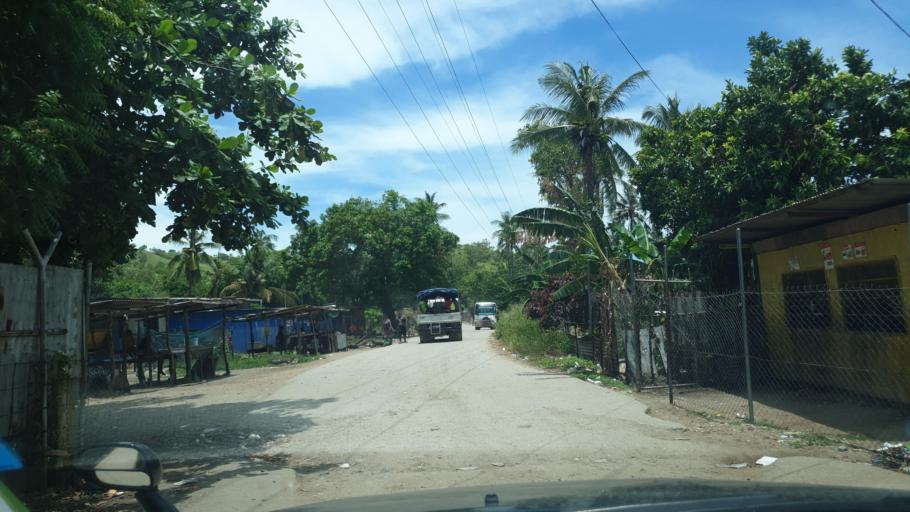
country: PG
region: National Capital
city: Port Moresby
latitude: -9.4192
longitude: 147.0447
